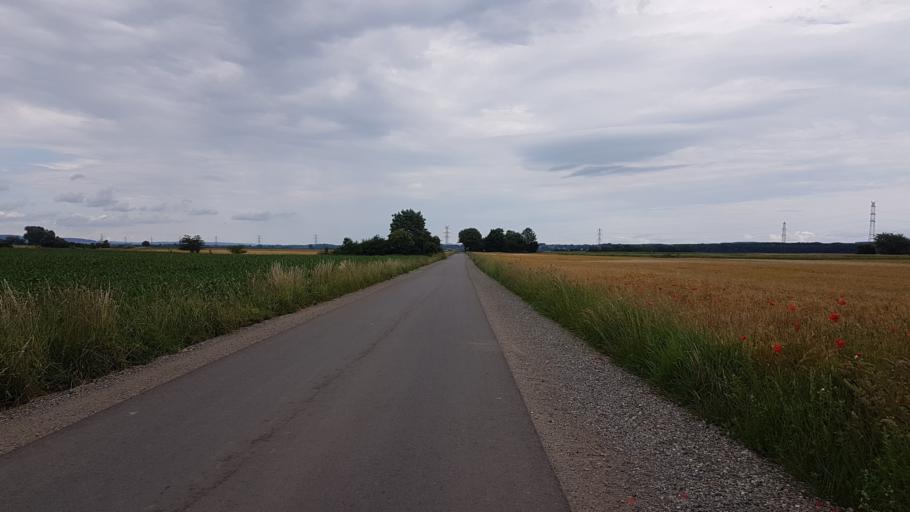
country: DE
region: Baden-Wuerttemberg
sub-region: Tuebingen Region
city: Herbertingen
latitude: 48.0765
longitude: 9.4125
